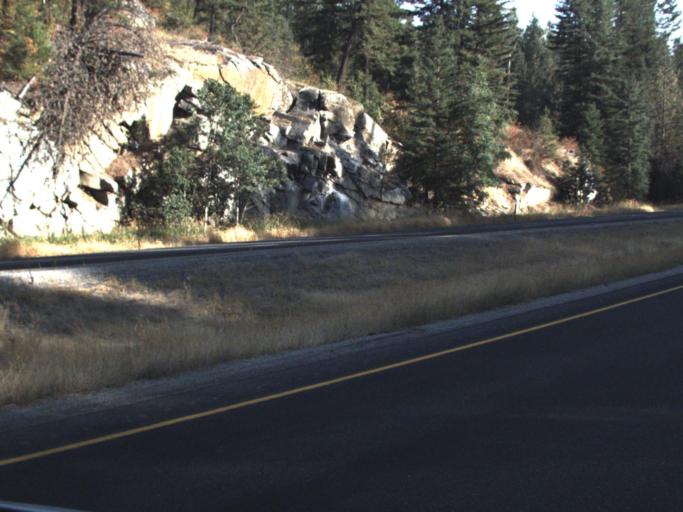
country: US
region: Washington
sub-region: Spokane County
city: Deer Park
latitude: 48.0888
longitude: -117.3263
